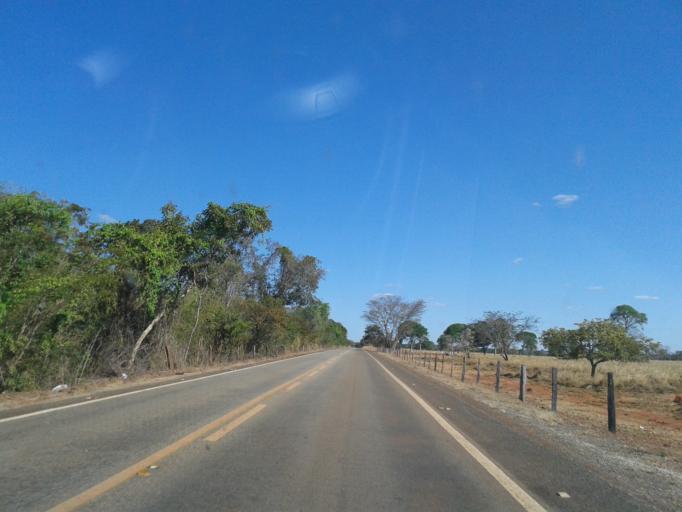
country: BR
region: Goias
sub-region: Mozarlandia
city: Mozarlandia
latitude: -14.2810
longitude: -50.4011
